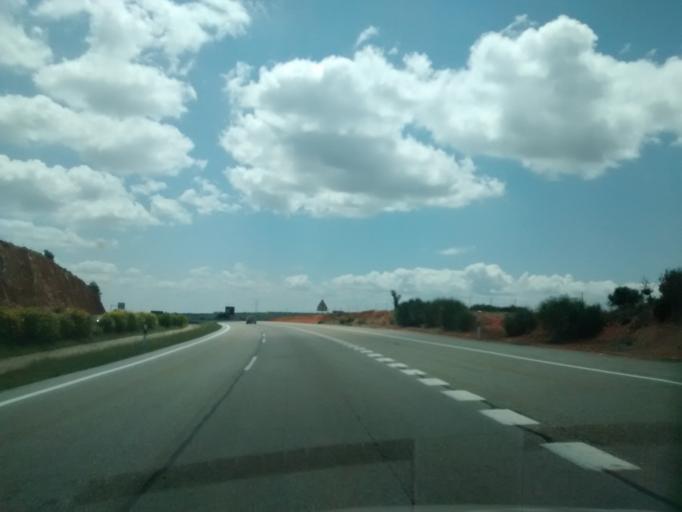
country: ES
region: Castille and Leon
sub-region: Provincia de Leon
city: Brazuelo
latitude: 42.4900
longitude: -6.1274
